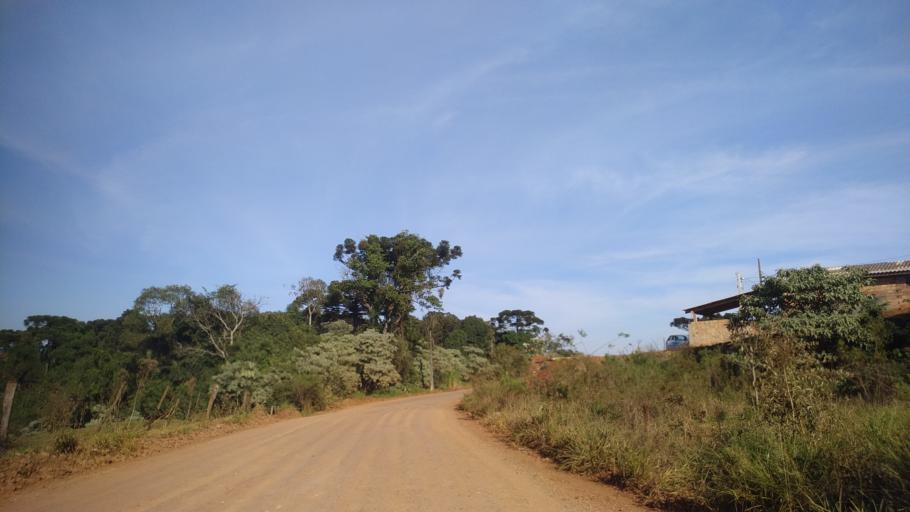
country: BR
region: Santa Catarina
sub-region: Chapeco
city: Chapeco
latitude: -27.1250
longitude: -52.6264
